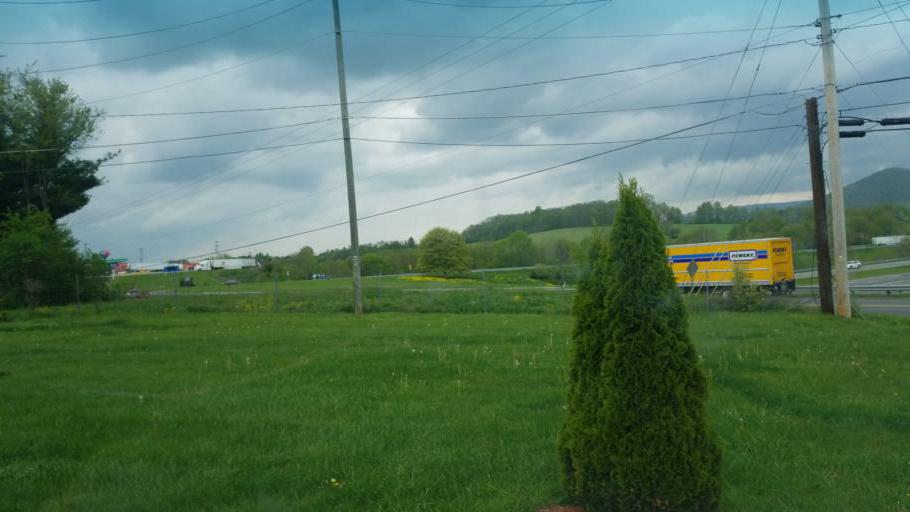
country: US
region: Virginia
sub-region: Wythe County
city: Wytheville
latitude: 36.9670
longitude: -81.0652
